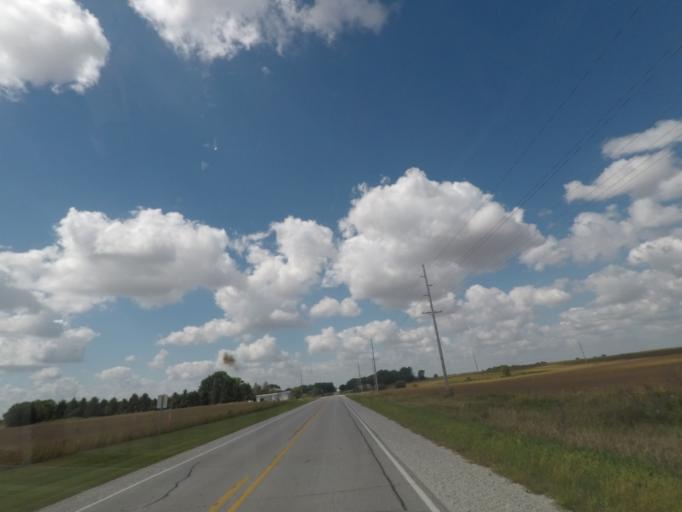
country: US
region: Iowa
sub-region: Story County
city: Nevada
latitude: 42.0225
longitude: -93.3259
